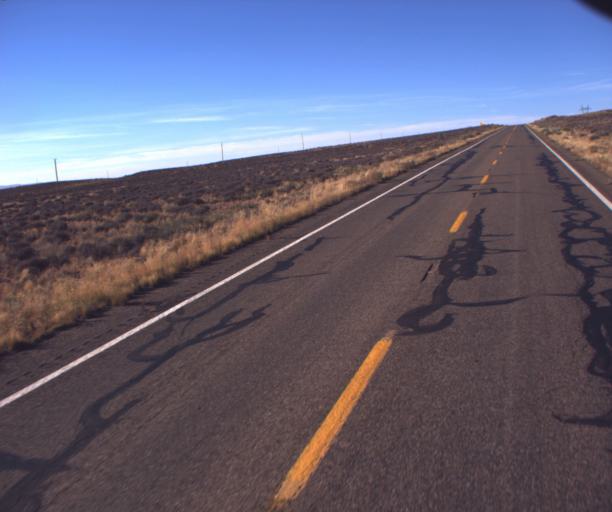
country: US
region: Arizona
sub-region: Coconino County
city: LeChee
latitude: 36.7901
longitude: -111.2960
